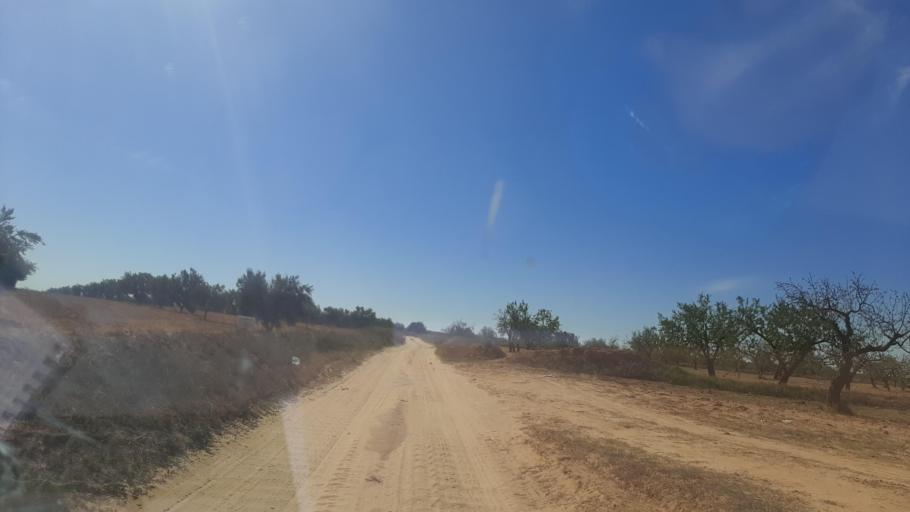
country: TN
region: Safaqis
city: Sfax
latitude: 34.8232
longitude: 10.5529
